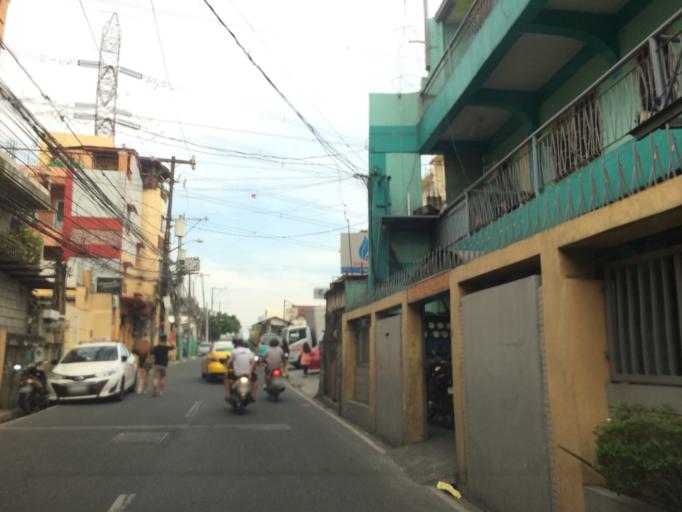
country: PH
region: Calabarzon
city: Bagong Pagasa
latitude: 14.6690
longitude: 121.0153
